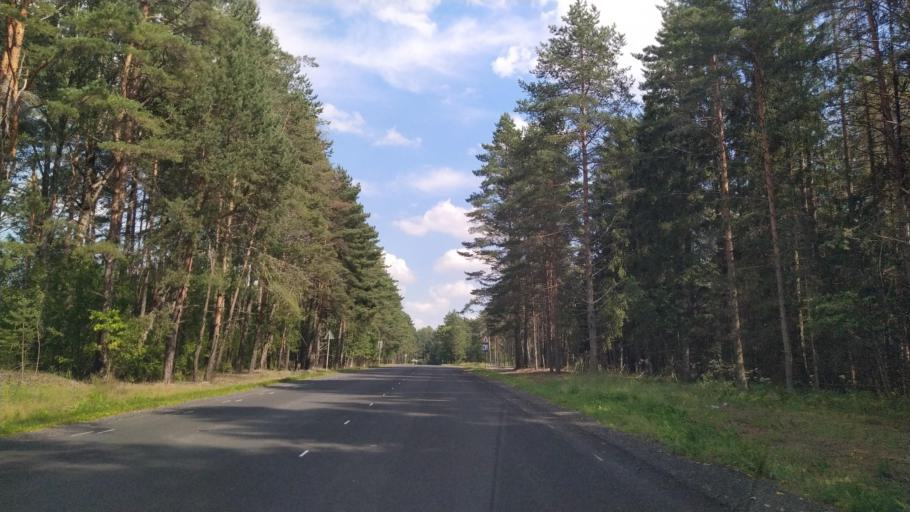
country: RU
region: Pskov
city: Porkhov
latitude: 57.7168
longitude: 29.2187
